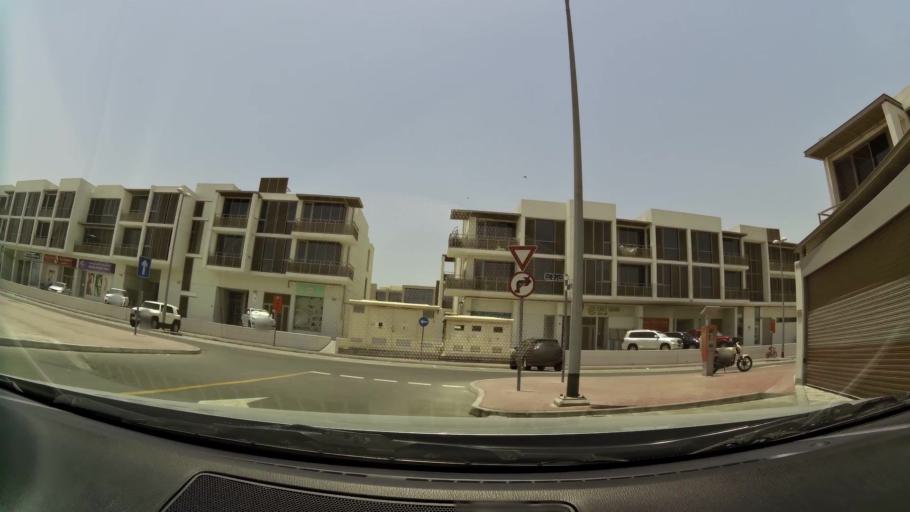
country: AE
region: Dubai
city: Dubai
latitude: 25.1851
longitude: 55.2395
